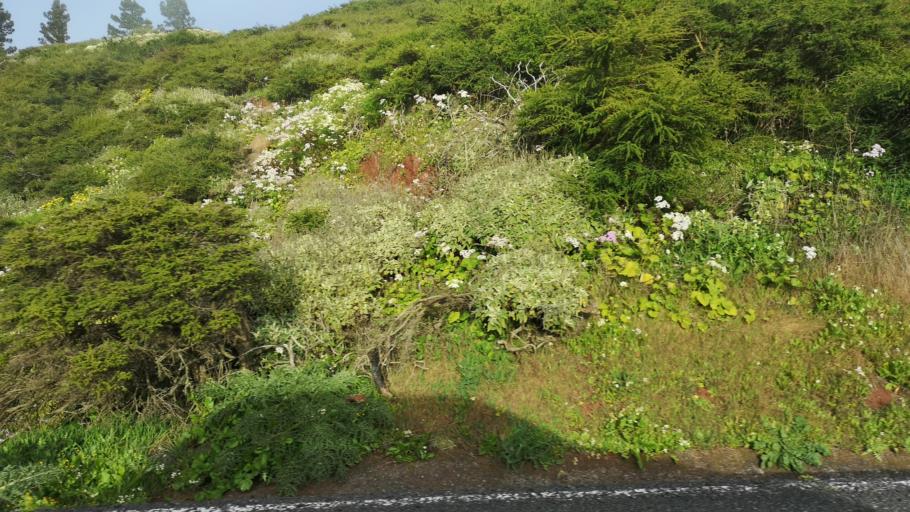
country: ES
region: Canary Islands
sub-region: Provincia de Santa Cruz de Tenerife
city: Alajero
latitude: 28.0956
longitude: -17.2470
